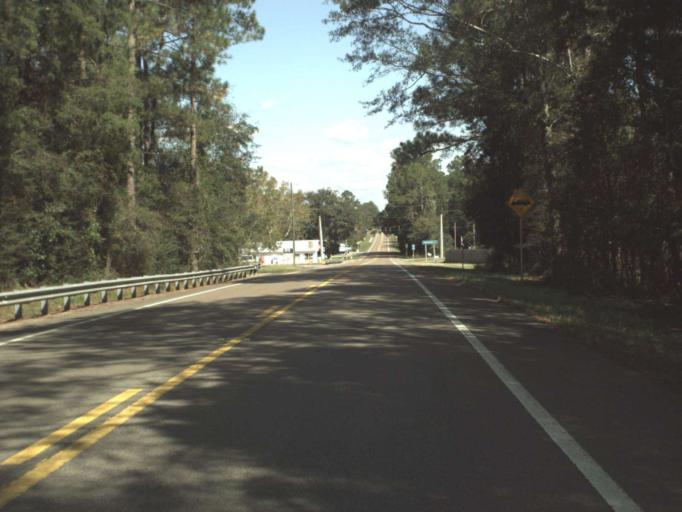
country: US
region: Alabama
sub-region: Geneva County
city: Samson
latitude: 30.9690
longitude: -86.1358
